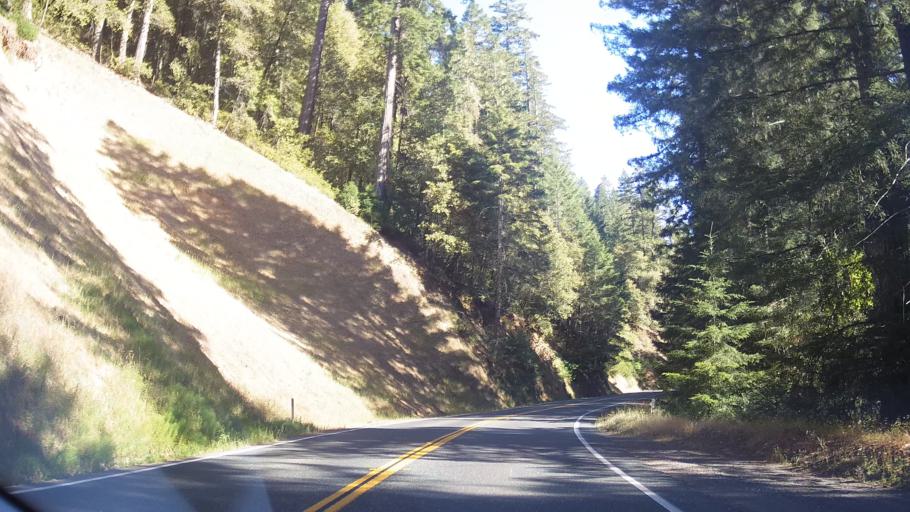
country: US
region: California
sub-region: Mendocino County
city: Brooktrails
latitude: 39.3576
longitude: -123.5092
